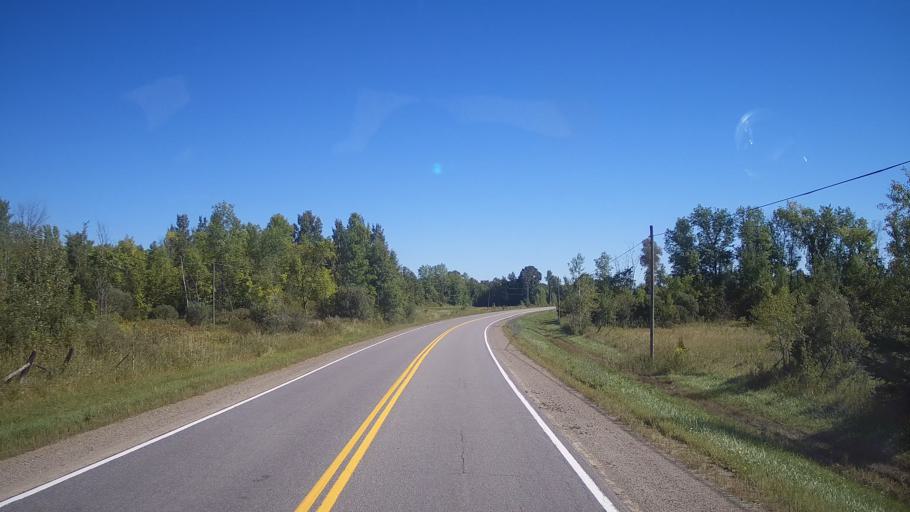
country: CA
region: Ontario
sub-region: Lanark County
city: Smiths Falls
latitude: 44.8113
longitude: -75.9665
